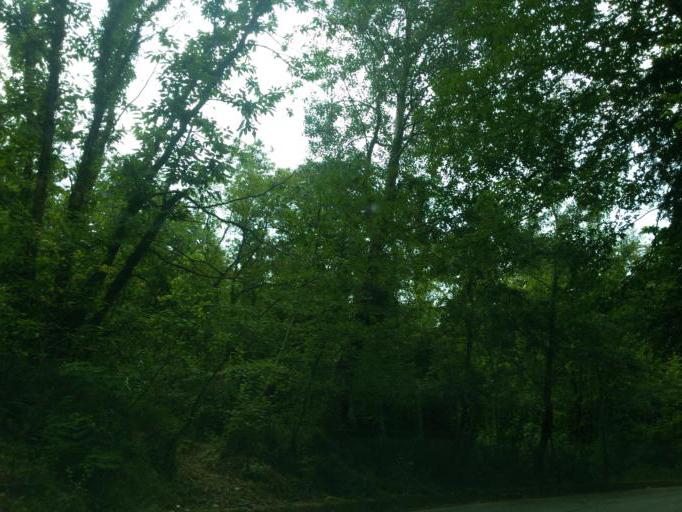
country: IT
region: Liguria
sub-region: Provincia di Genova
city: Piccarello
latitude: 44.4388
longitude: 9.0093
